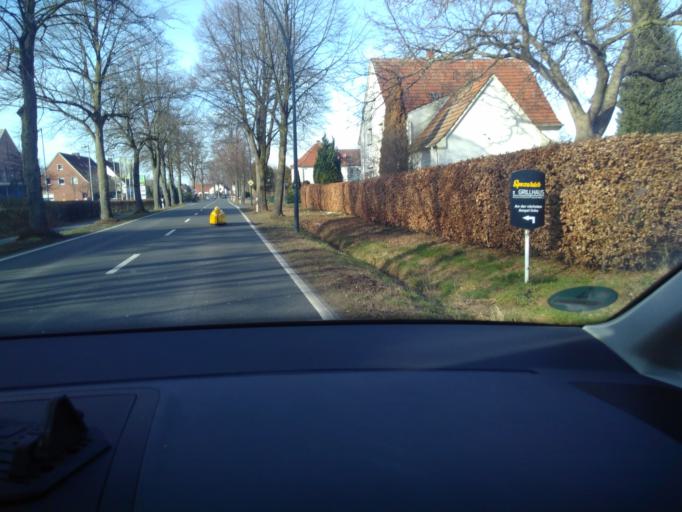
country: DE
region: North Rhine-Westphalia
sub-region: Regierungsbezirk Detmold
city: Guetersloh
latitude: 51.8805
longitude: 8.3936
